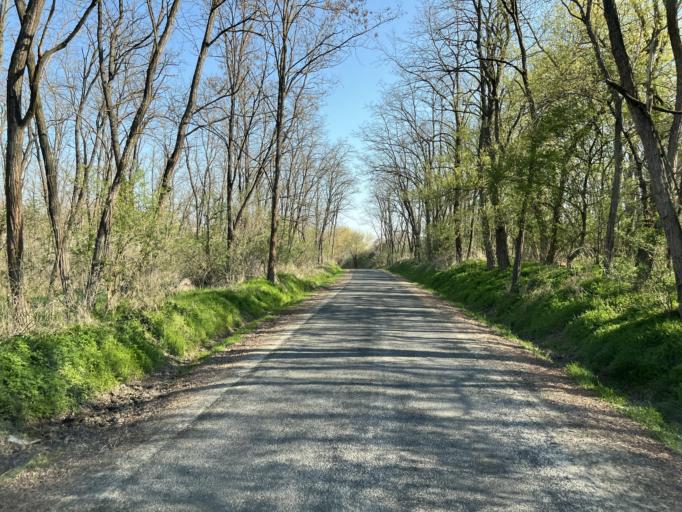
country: SK
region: Nitriansky
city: Sahy
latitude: 48.0236
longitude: 18.8272
